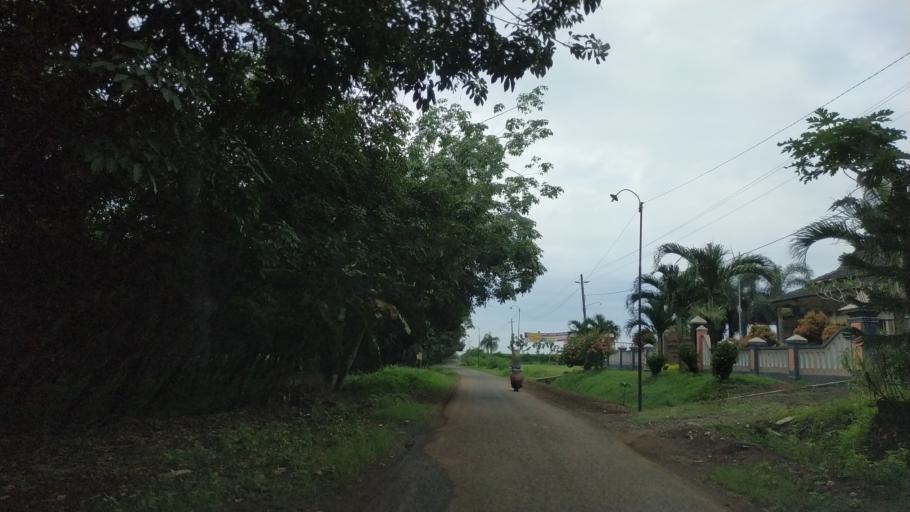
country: ID
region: Central Java
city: Krajan Tegalombo
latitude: -6.4300
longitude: 110.9834
